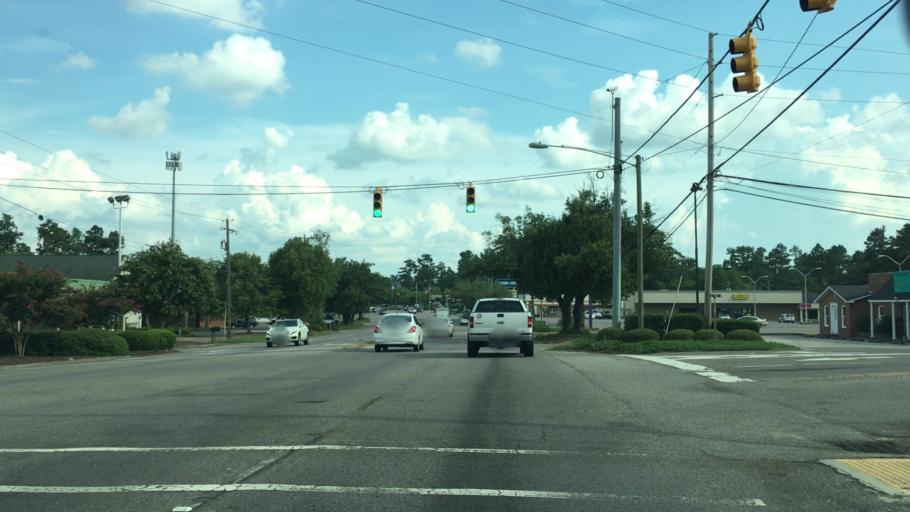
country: US
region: South Carolina
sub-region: Aiken County
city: Aiken
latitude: 33.5333
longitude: -81.7245
